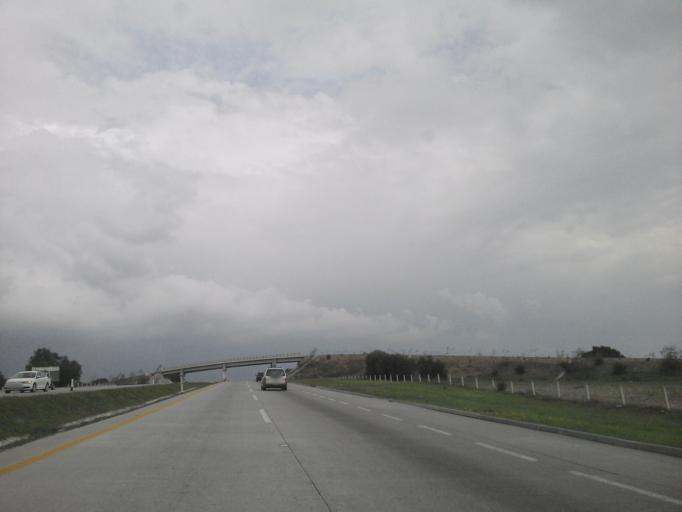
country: MX
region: Mexico
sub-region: Apaxco
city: Colonia Juarez
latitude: 19.9808
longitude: -99.1178
